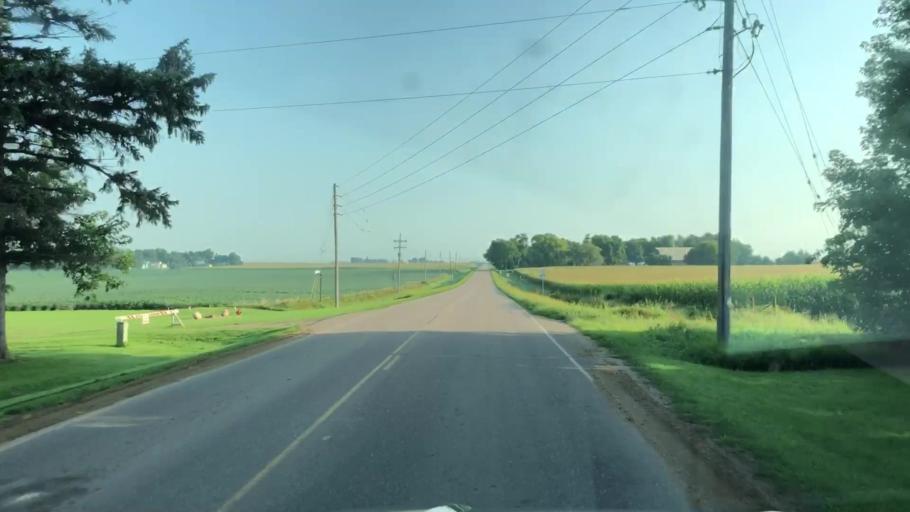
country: US
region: Iowa
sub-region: Sioux County
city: Hull
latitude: 43.1933
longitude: -96.0003
